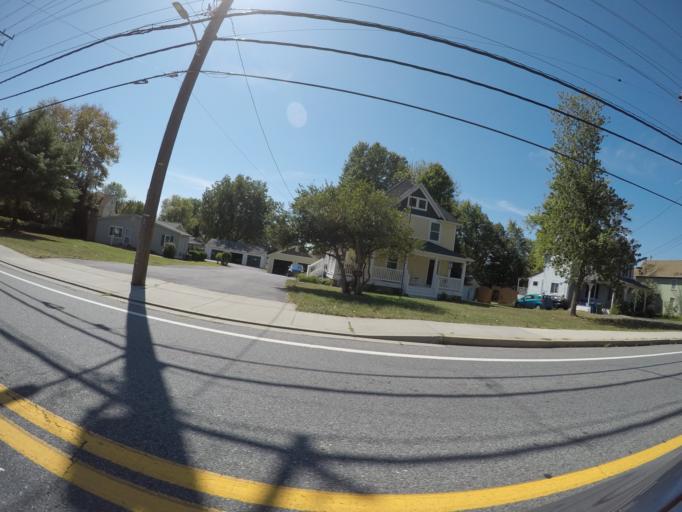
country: US
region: Maryland
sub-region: Harford County
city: Aberdeen
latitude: 39.5164
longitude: -76.1790
